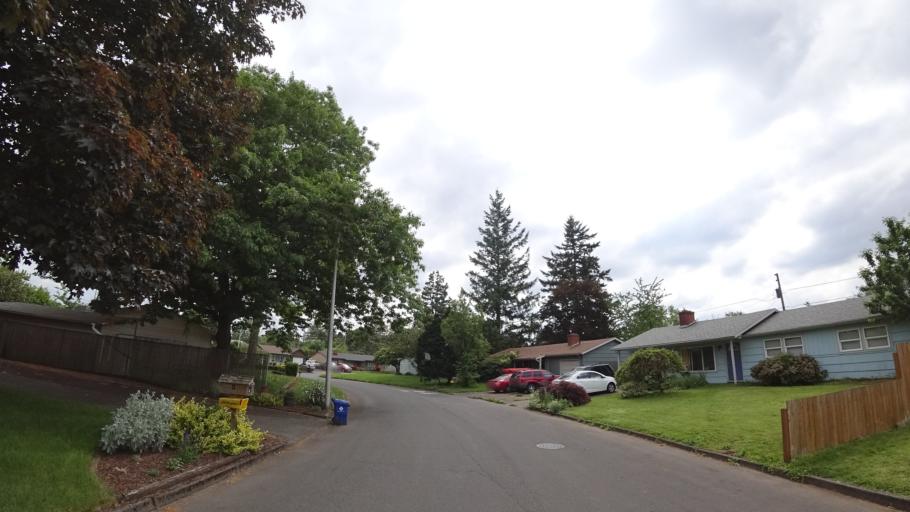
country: US
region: Oregon
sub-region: Multnomah County
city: Gresham
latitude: 45.5062
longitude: -122.4781
